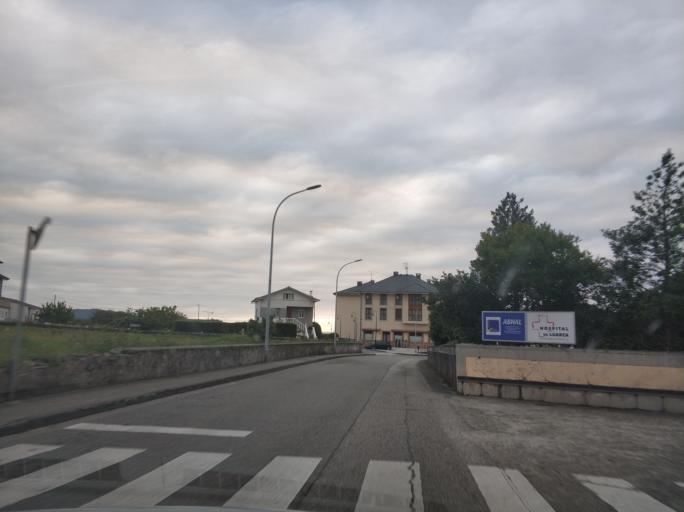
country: ES
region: Asturias
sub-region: Province of Asturias
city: Navia
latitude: 43.5449
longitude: -6.5288
